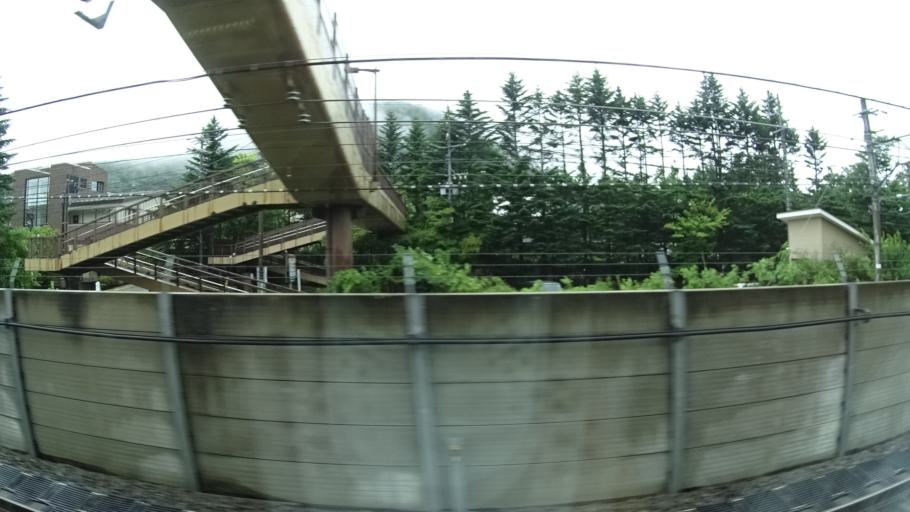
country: JP
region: Nagano
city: Saku
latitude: 36.3428
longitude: 138.6124
